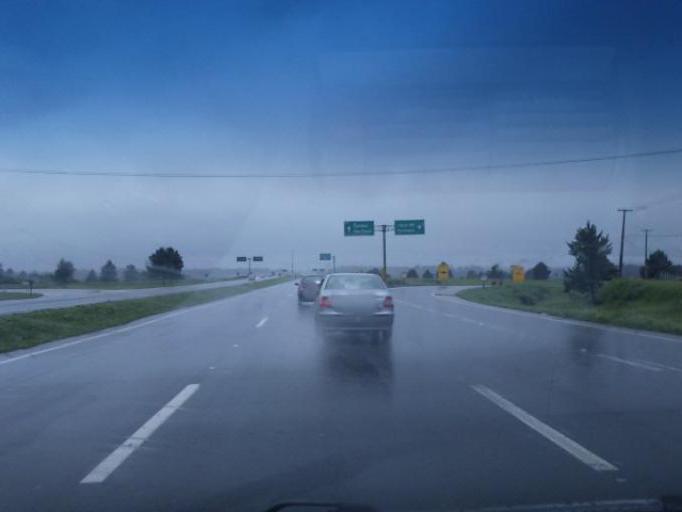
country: BR
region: Parana
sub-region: Sao Jose Dos Pinhais
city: Sao Jose dos Pinhais
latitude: -25.5147
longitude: -49.1303
